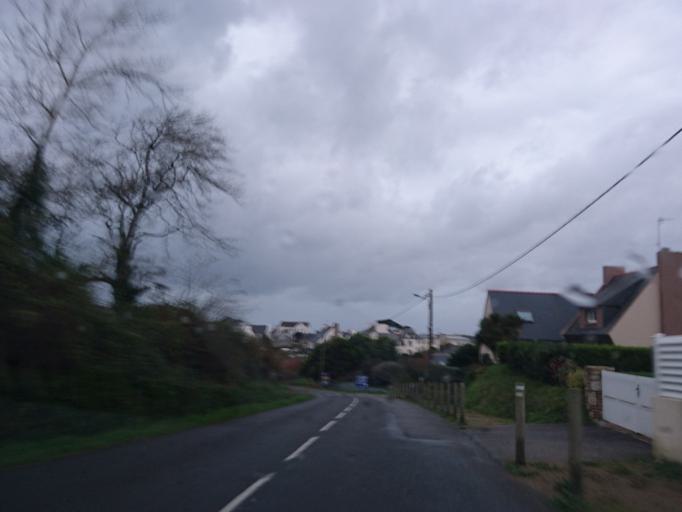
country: FR
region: Brittany
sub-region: Departement du Finistere
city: Le Conquet
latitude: 48.3561
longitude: -4.7752
